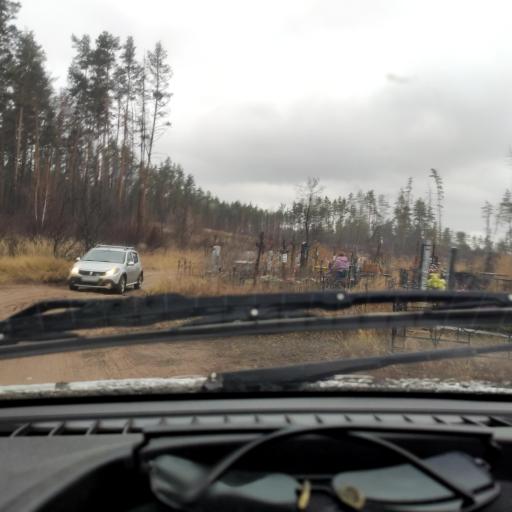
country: RU
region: Samara
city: Zhigulevsk
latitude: 53.5374
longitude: 49.5548
